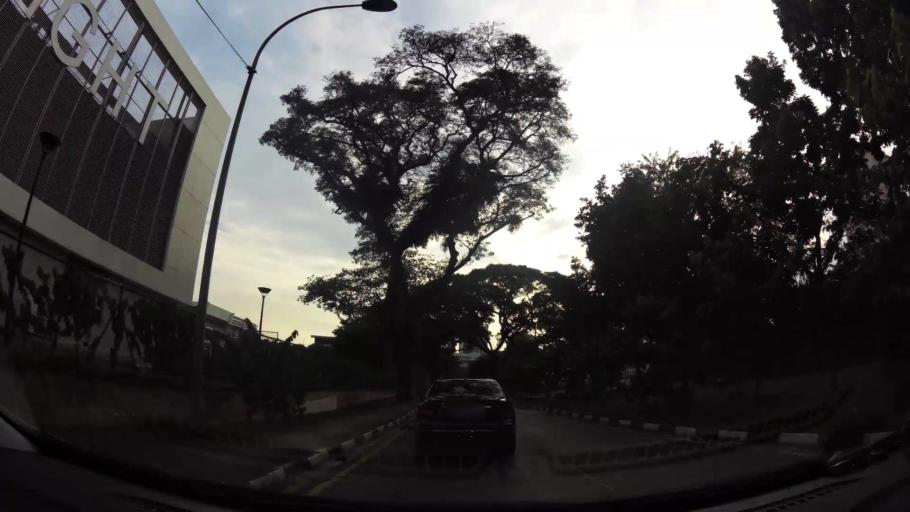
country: SG
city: Singapore
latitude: 1.3202
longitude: 103.8554
